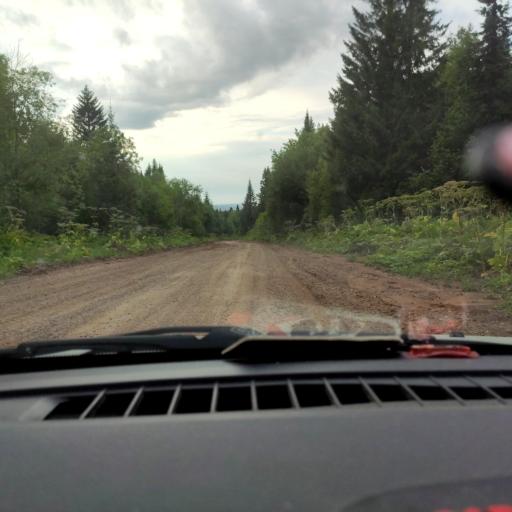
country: RU
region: Perm
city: Kultayevo
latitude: 57.8128
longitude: 56.0029
